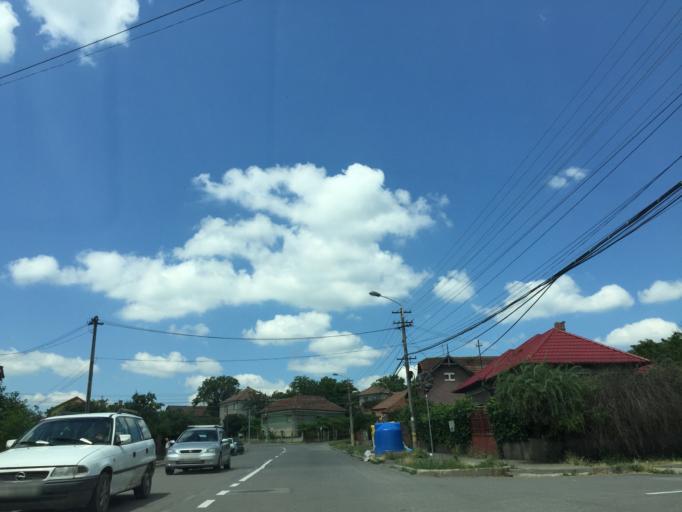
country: RO
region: Cluj
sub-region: Municipiul Cluj-Napoca
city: Cluj-Napoca
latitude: 46.7894
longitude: 23.5754
